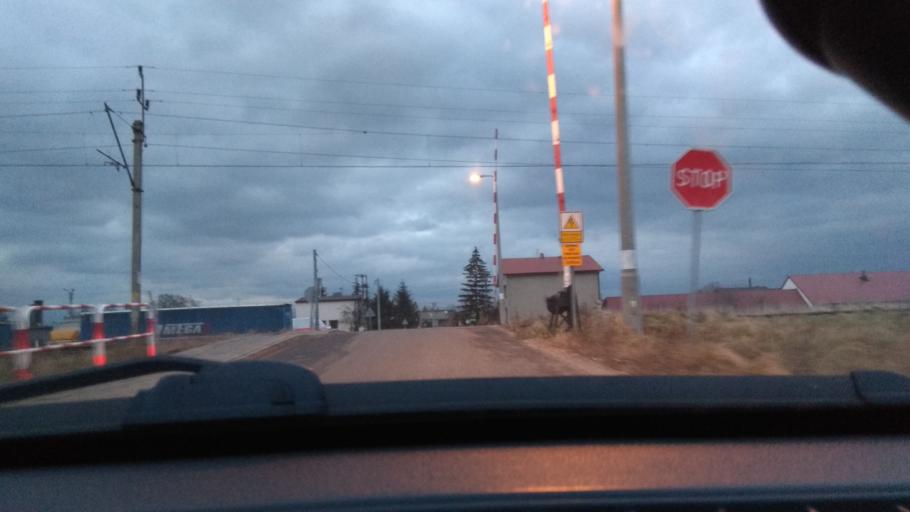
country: PL
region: Greater Poland Voivodeship
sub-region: Powiat kepinski
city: Slupia pod Kepnem
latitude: 51.3007
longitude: 18.0787
